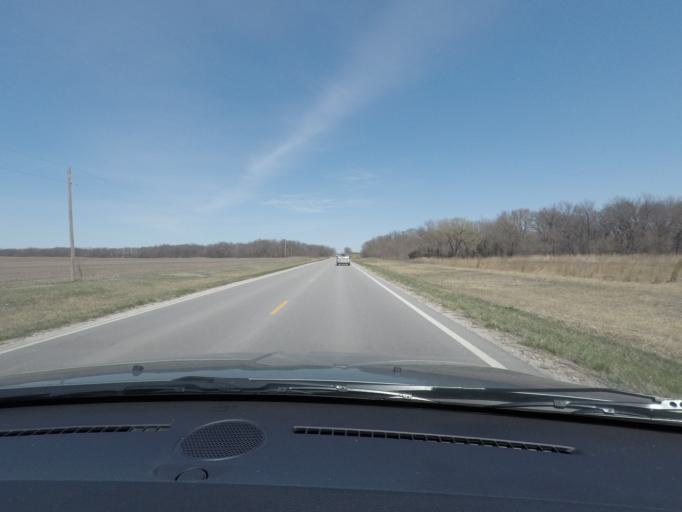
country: US
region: Kansas
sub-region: Lyon County
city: Emporia
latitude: 38.4654
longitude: -96.1712
